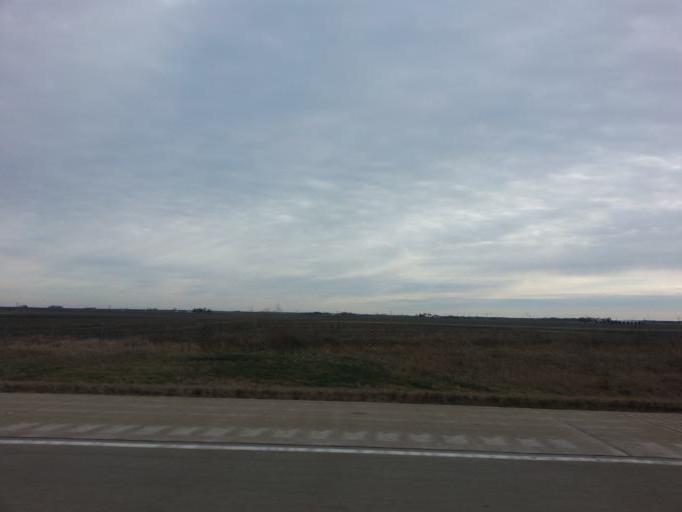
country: US
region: Illinois
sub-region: Woodford County
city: El Paso
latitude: 40.6965
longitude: -89.0290
